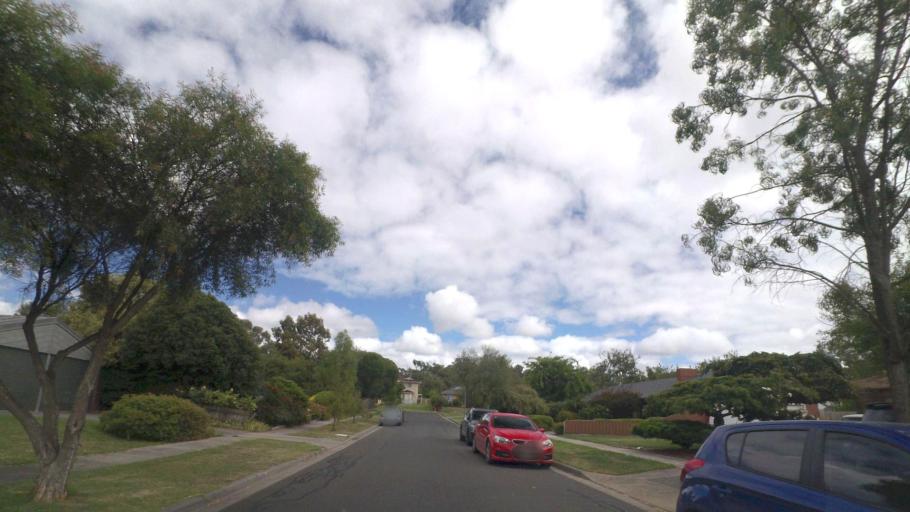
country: AU
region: Victoria
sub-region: Maroondah
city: Bayswater North
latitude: -37.8307
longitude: 145.3044
